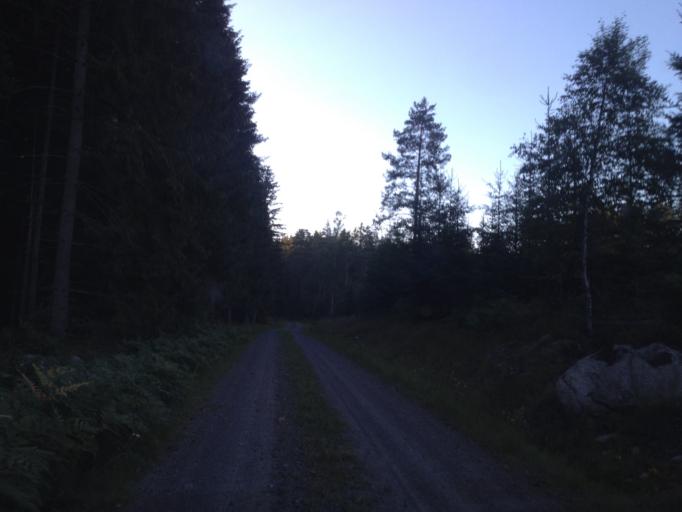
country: SE
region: Kalmar
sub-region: Vasterviks Kommun
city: Overum
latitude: 58.0038
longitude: 16.1220
